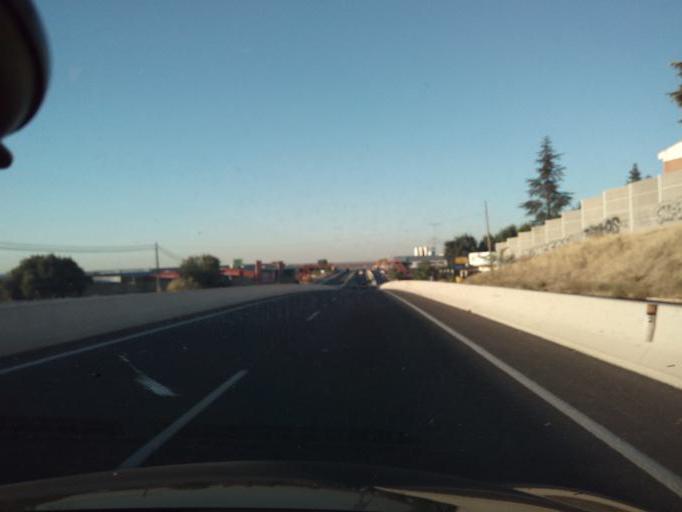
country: ES
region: Madrid
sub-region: Provincia de Madrid
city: Ajalvir
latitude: 40.5166
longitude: -3.4810
